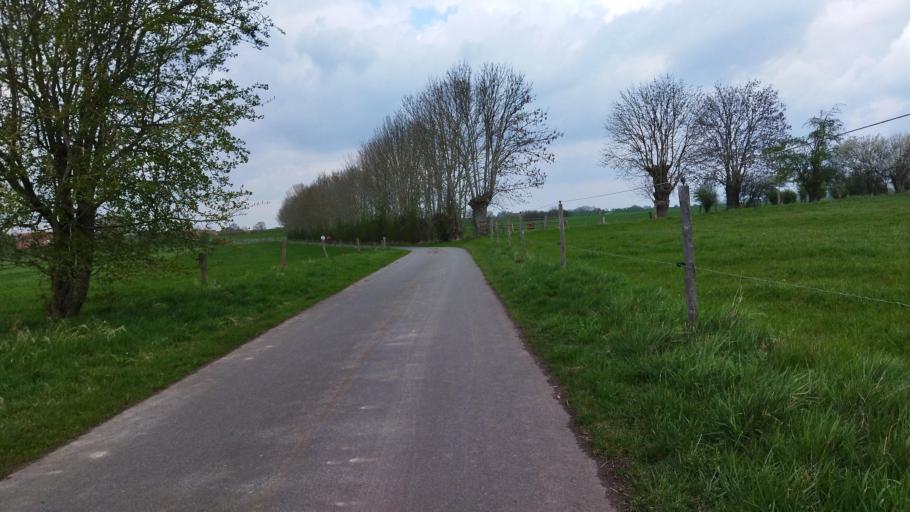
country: DE
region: Lower Saxony
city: Blender
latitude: 52.9079
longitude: 9.1647
